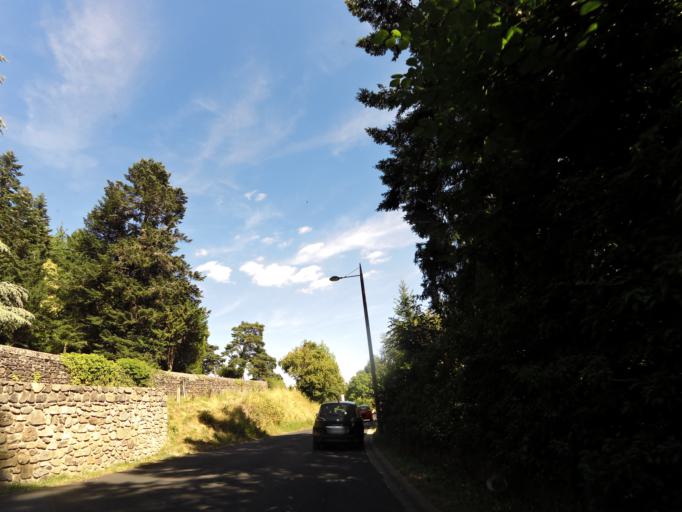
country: FR
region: Auvergne
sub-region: Departement du Puy-de-Dome
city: Aydat
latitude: 45.5757
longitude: 2.9451
